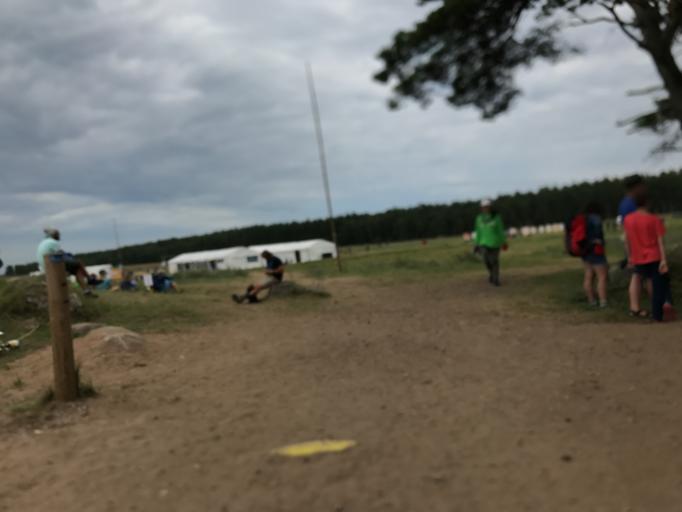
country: SE
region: Skane
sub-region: Kristianstads Kommun
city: Fjalkinge
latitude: 56.0059
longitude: 14.3059
